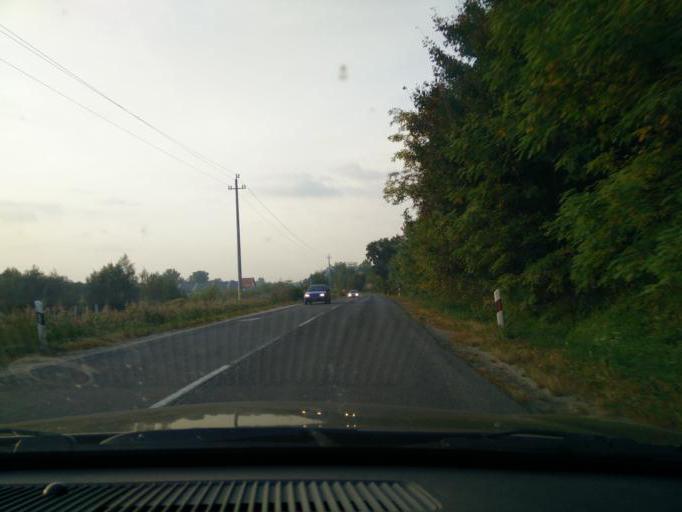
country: HU
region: Pest
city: Piliscsaba
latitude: 47.6392
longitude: 18.8143
